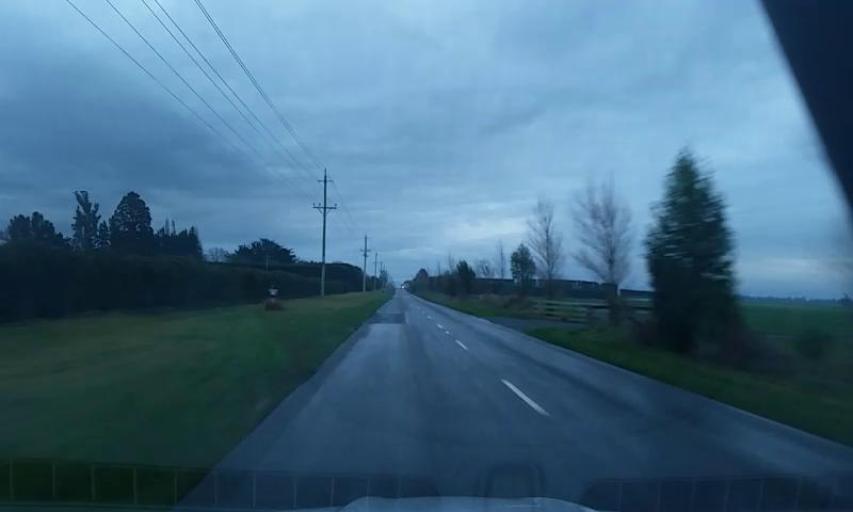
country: NZ
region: Canterbury
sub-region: Ashburton District
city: Rakaia
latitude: -43.7581
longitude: 171.9506
